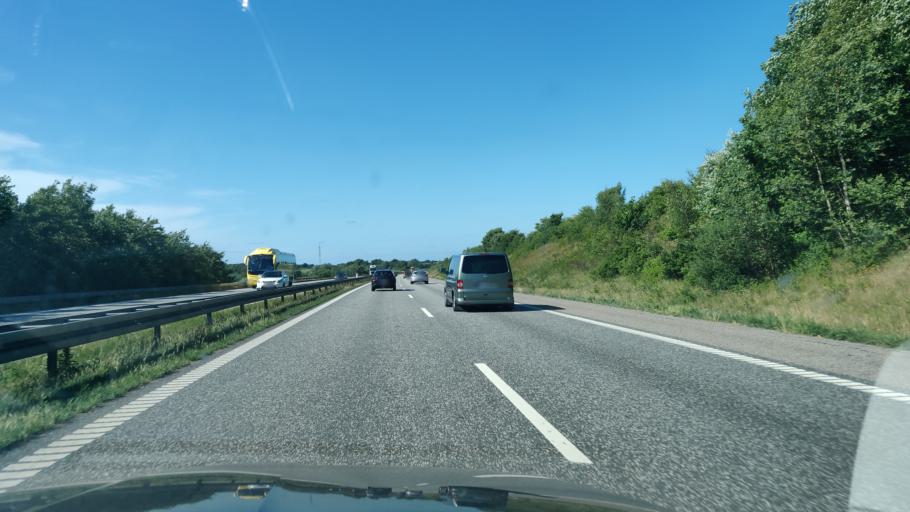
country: DK
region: North Denmark
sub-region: Mariagerfjord Kommune
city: Hobro
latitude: 56.6894
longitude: 9.7297
